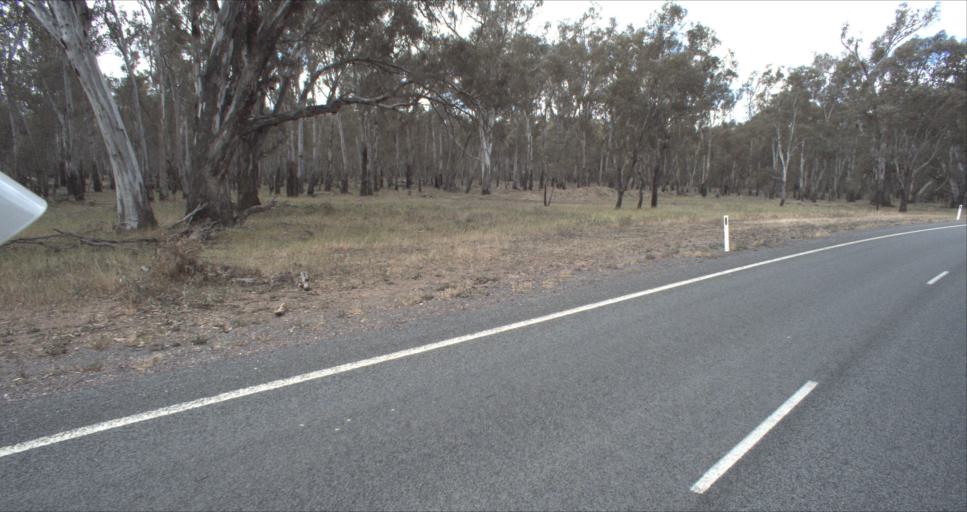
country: AU
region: New South Wales
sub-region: Leeton
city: Leeton
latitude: -34.6410
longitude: 146.3595
